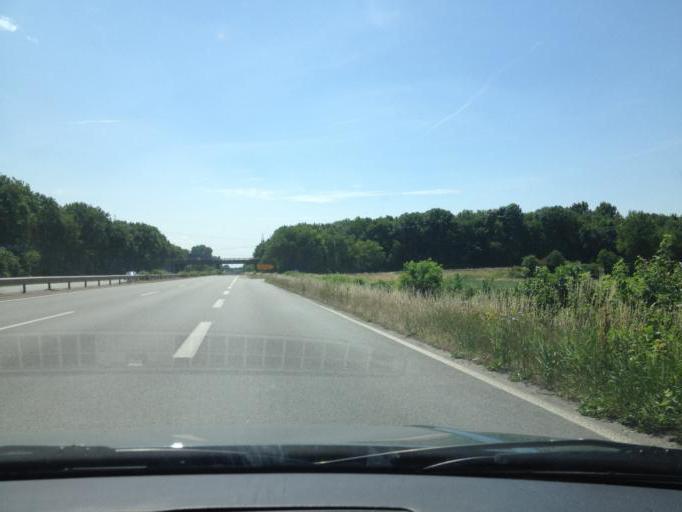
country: DE
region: Rheinland-Pfalz
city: Limburgerhof
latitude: 49.4373
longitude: 8.4069
